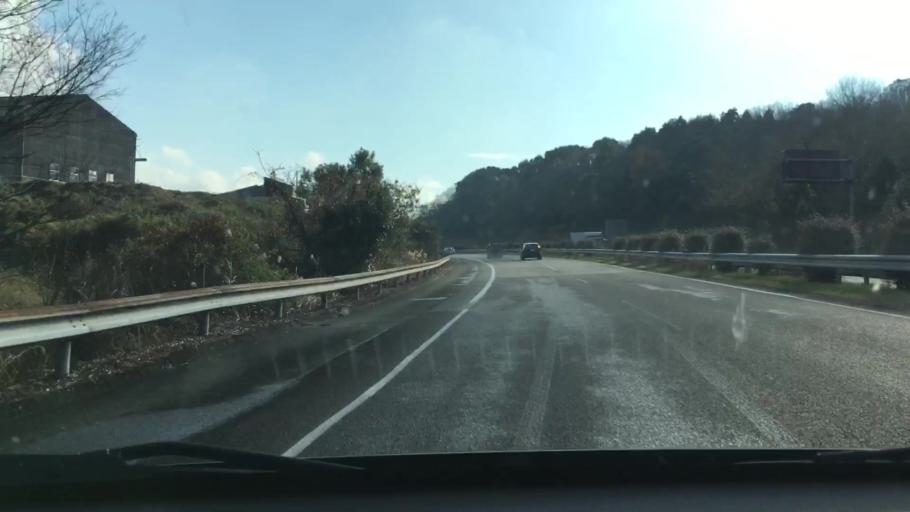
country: JP
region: Kumamoto
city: Matsubase
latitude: 32.6434
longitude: 130.7066
